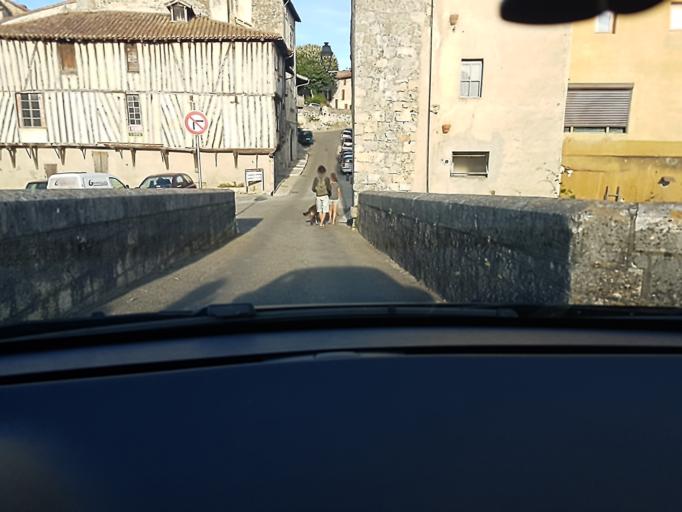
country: FR
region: Aquitaine
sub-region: Departement du Lot-et-Garonne
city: Nerac
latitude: 44.1367
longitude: 0.3417
